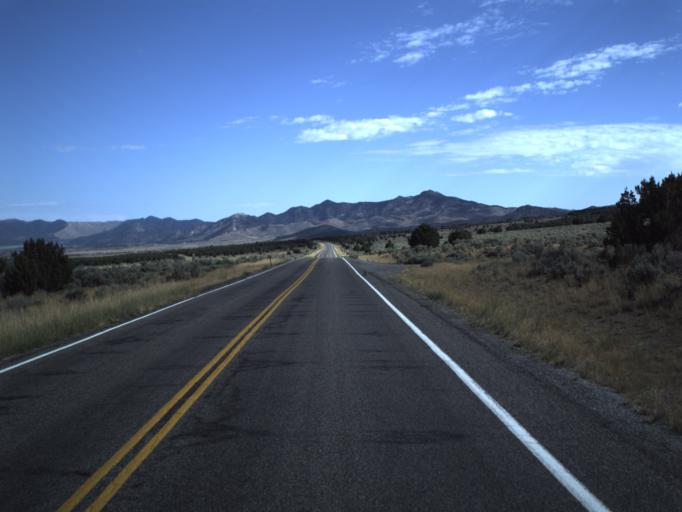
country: US
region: Utah
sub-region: Juab County
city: Mona
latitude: 39.8250
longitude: -112.1404
